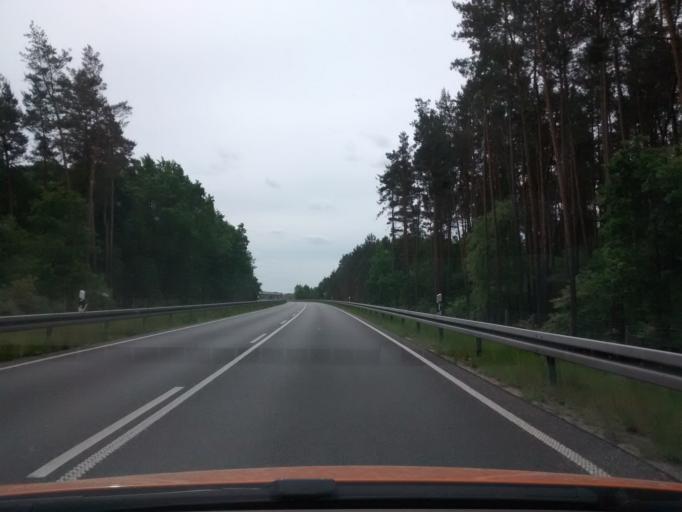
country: DE
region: Brandenburg
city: Juterbog
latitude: 52.0472
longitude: 13.1044
